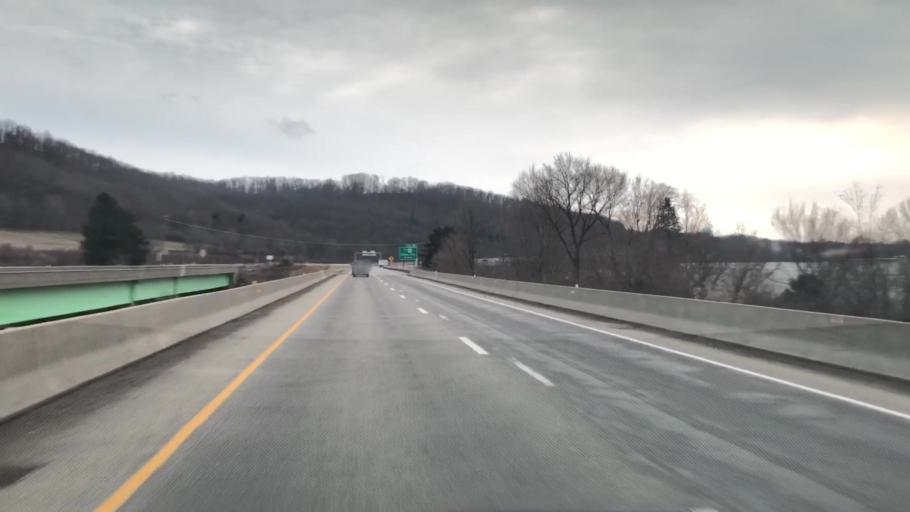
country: US
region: Pennsylvania
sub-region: Butler County
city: Zelienople
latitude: 40.8024
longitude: -80.1181
